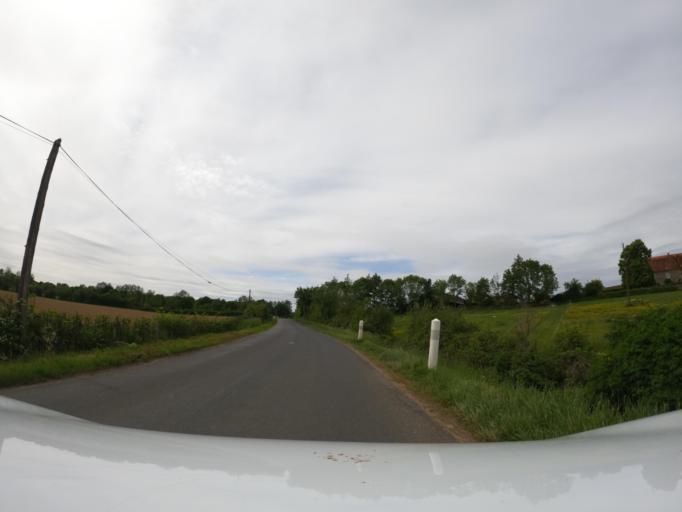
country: FR
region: Pays de la Loire
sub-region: Departement de la Vendee
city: Foussais-Payre
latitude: 46.5129
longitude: -0.6489
